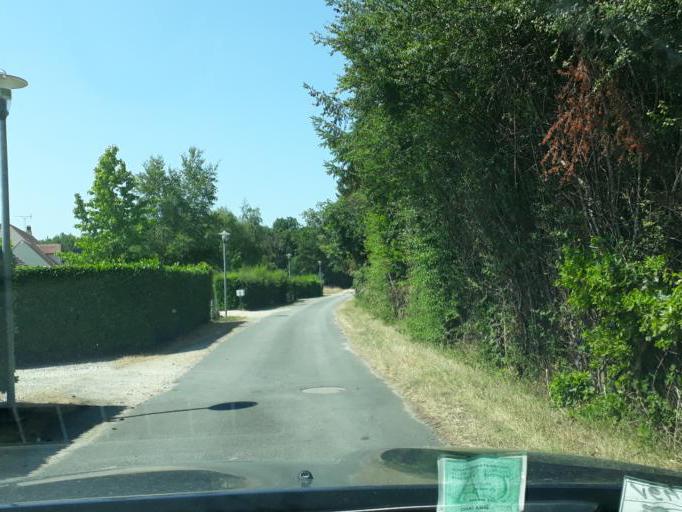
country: FR
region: Centre
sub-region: Departement du Loir-et-Cher
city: Vouzon
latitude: 47.6417
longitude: 2.0496
